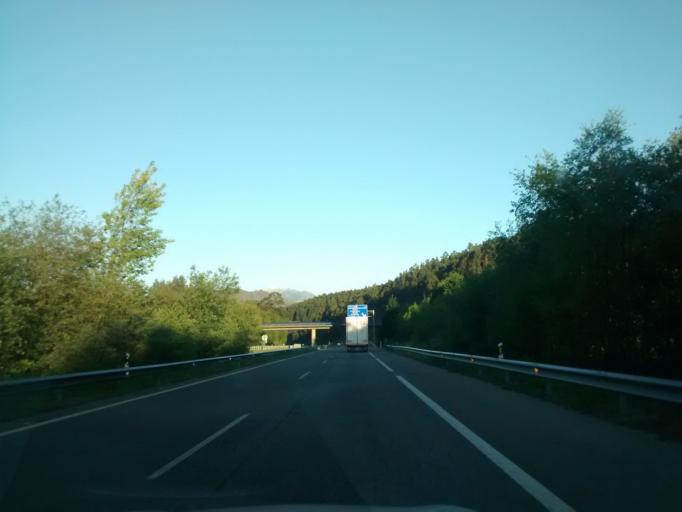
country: ES
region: Asturias
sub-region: Province of Asturias
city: Ribadesella
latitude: 43.4398
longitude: -5.0295
